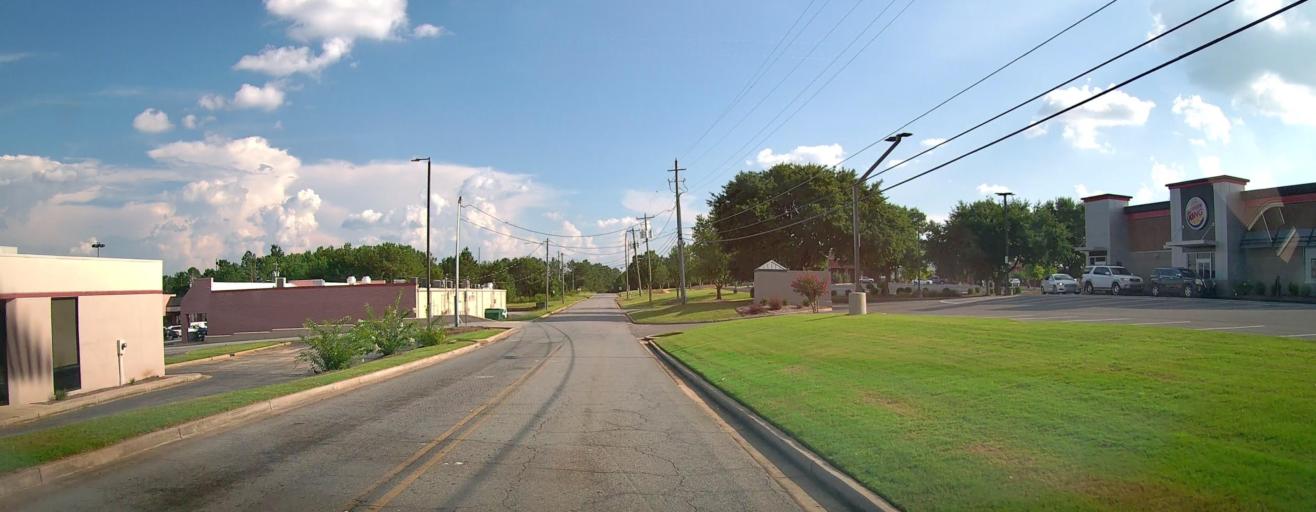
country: US
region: Georgia
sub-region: Houston County
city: Warner Robins
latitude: 32.5935
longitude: -83.6275
